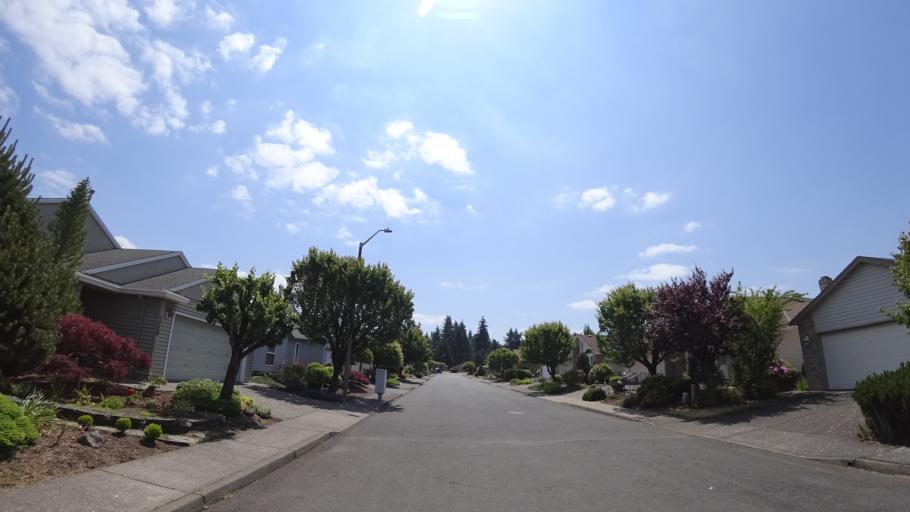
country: US
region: Oregon
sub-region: Multnomah County
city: Fairview
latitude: 45.5358
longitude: -122.5069
